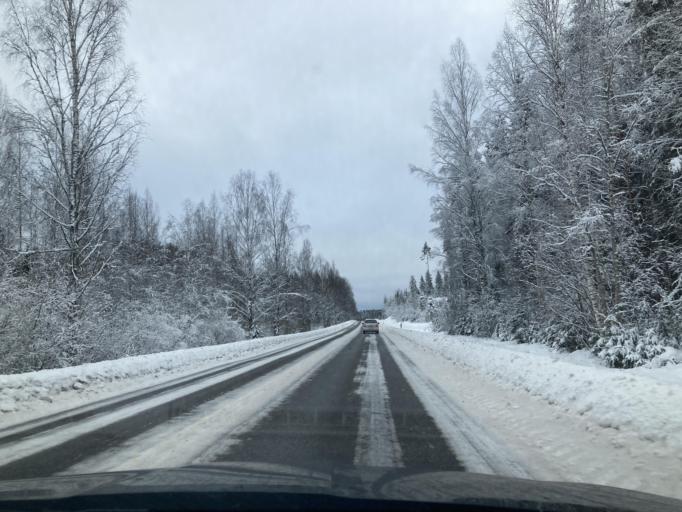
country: FI
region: Central Finland
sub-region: Jaemsae
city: Kuhmoinen
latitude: 61.5096
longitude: 25.1401
